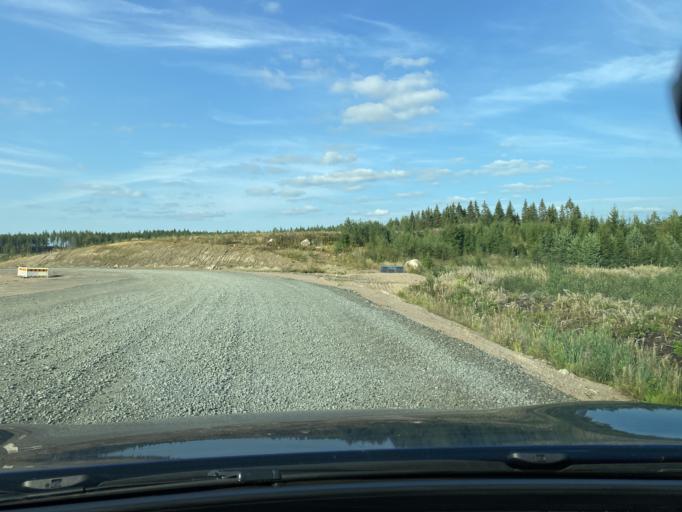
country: FI
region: Kymenlaakso
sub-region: Kouvola
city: Iitti
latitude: 60.8769
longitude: 26.4928
